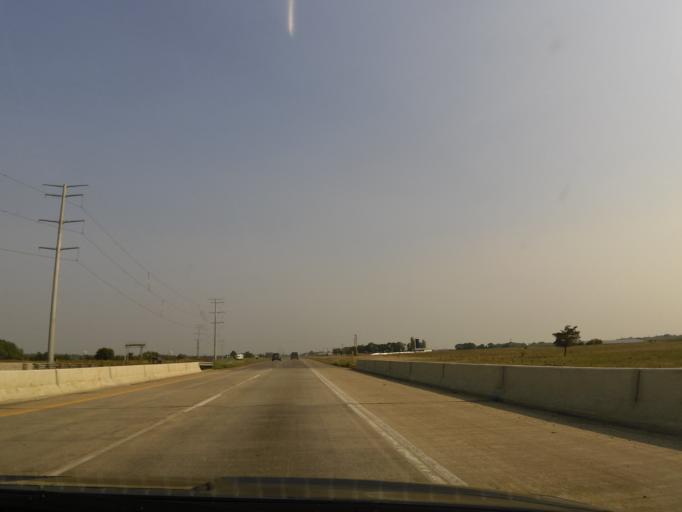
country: US
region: Minnesota
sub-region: Stearns County
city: Melrose
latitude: 45.6855
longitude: -94.8577
